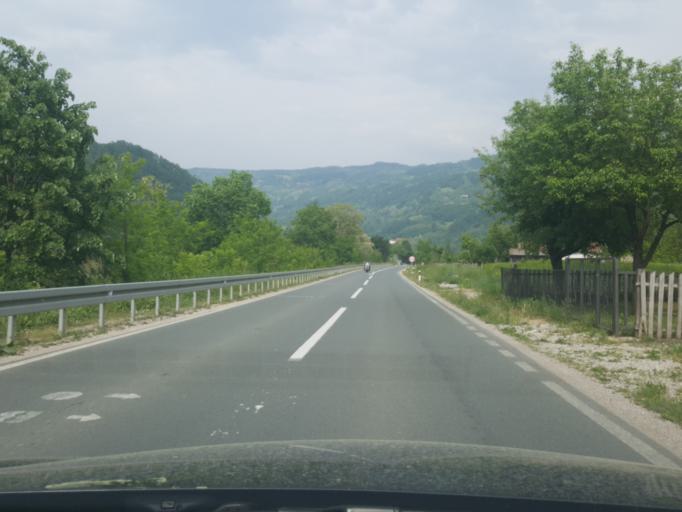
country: RS
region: Central Serbia
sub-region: Zlatiborski Okrug
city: Bajina Basta
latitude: 44.0105
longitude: 19.6046
